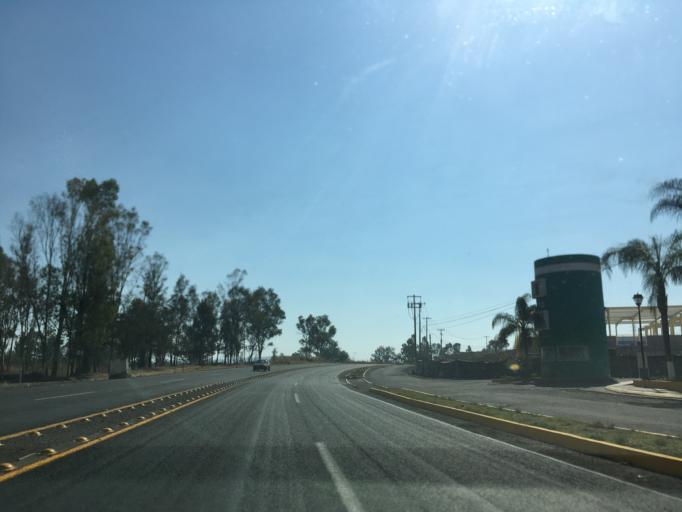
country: MX
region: Michoacan
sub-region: Morelia
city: La Aldea
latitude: 19.7340
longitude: -101.1303
